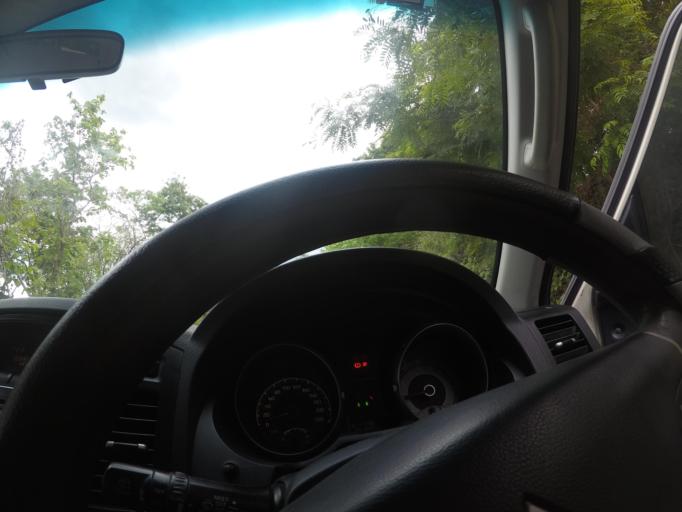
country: TL
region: Bobonaro
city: Maliana
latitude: -8.9721
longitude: 125.2296
